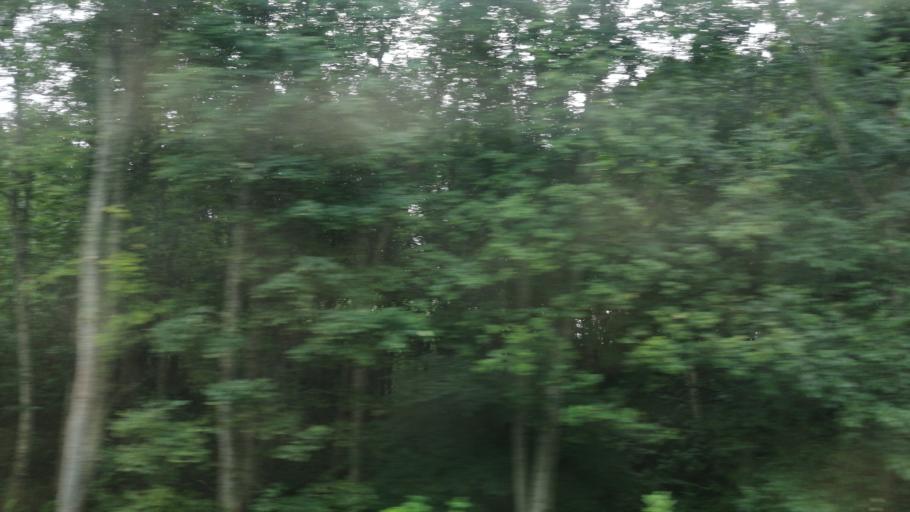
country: GB
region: Scotland
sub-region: Highland
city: Evanton
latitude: 57.6399
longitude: -4.3535
